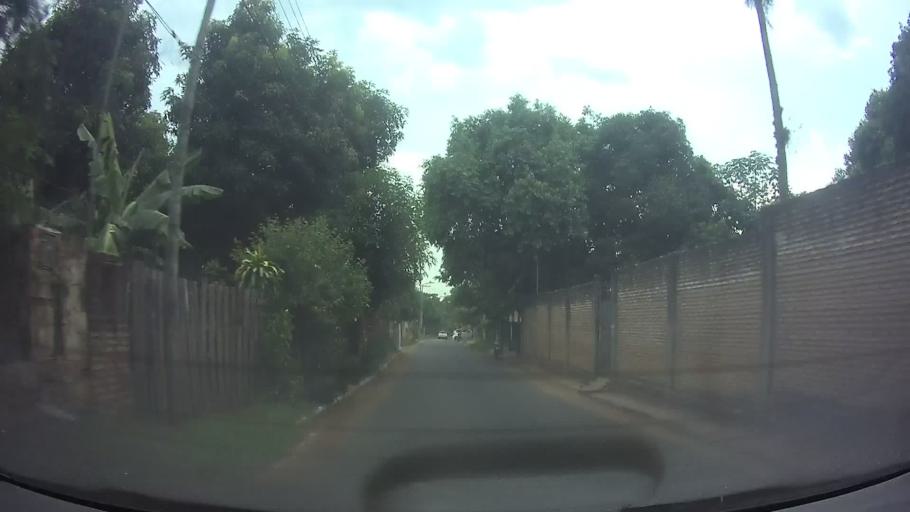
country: PY
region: Central
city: San Lorenzo
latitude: -25.2811
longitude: -57.4817
